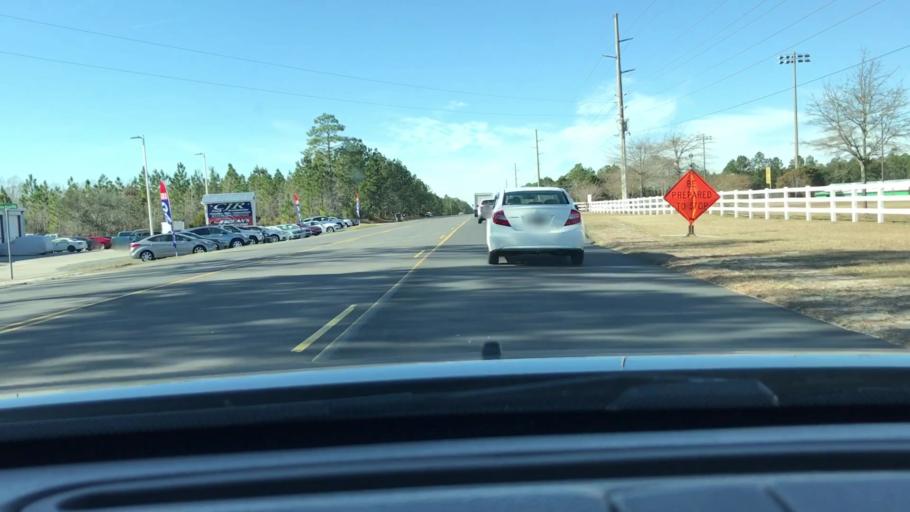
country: US
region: North Carolina
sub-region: Brunswick County
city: Shallotte
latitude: 33.9791
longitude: -78.4106
